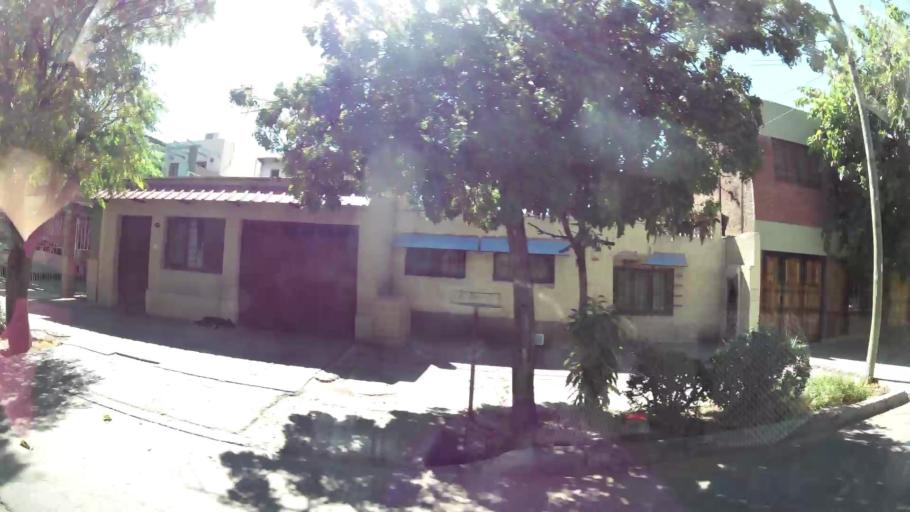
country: AR
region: Mendoza
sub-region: Departamento de Godoy Cruz
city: Godoy Cruz
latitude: -32.9046
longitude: -68.8564
